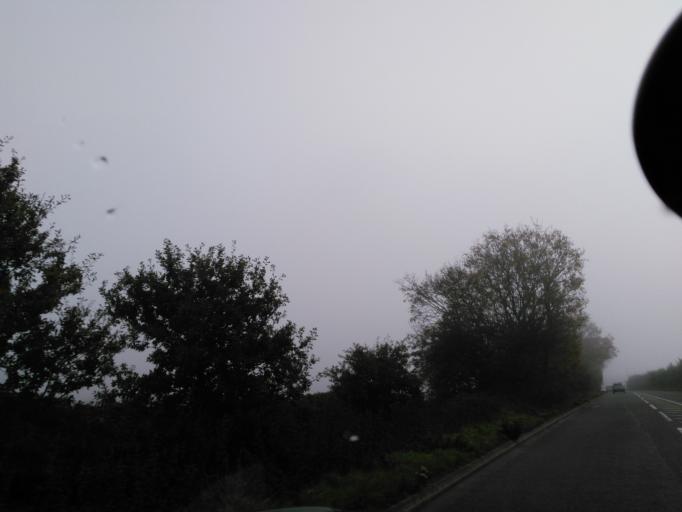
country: GB
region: England
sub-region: Wiltshire
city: Worton
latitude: 51.3503
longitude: -2.0443
